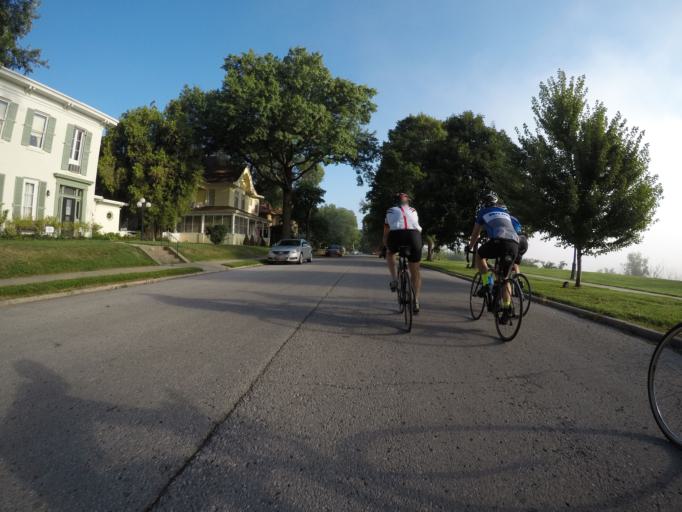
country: US
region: Kansas
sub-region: Leavenworth County
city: Leavenworth
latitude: 39.3222
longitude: -94.9103
